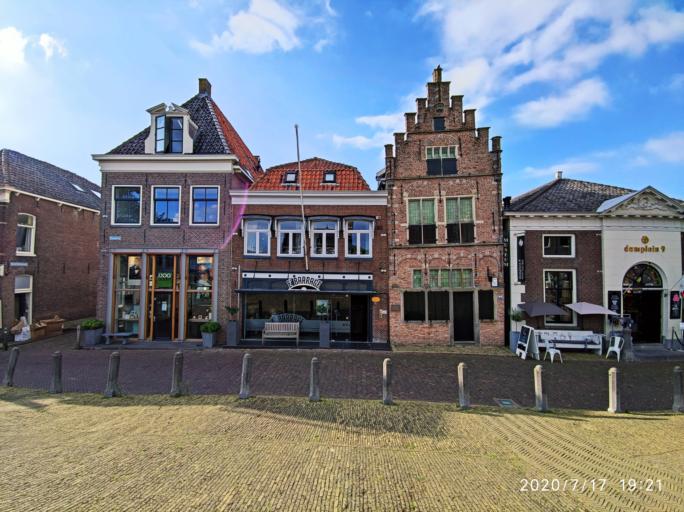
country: NL
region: North Holland
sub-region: Gemeente Edam-Volendam
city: Edam
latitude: 52.5125
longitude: 5.0490
